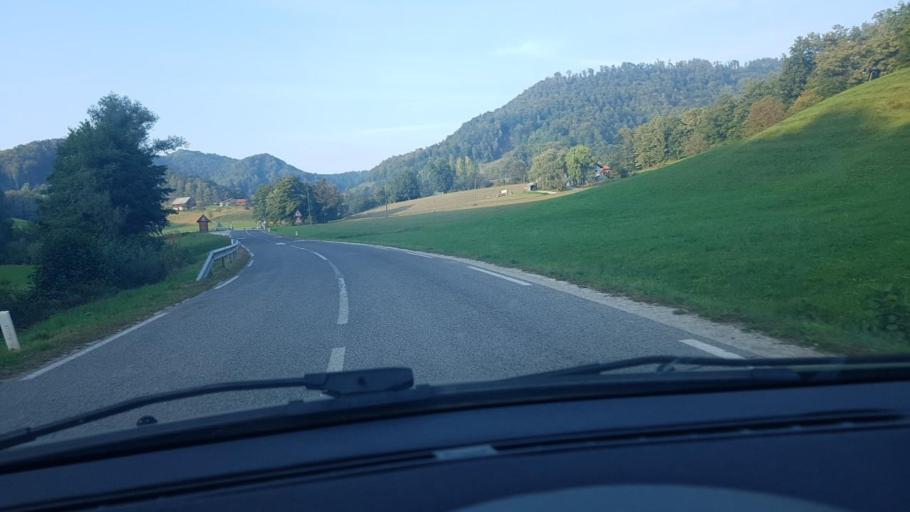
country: SI
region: Rogatec
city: Rogatec
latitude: 46.2500
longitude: 15.7010
